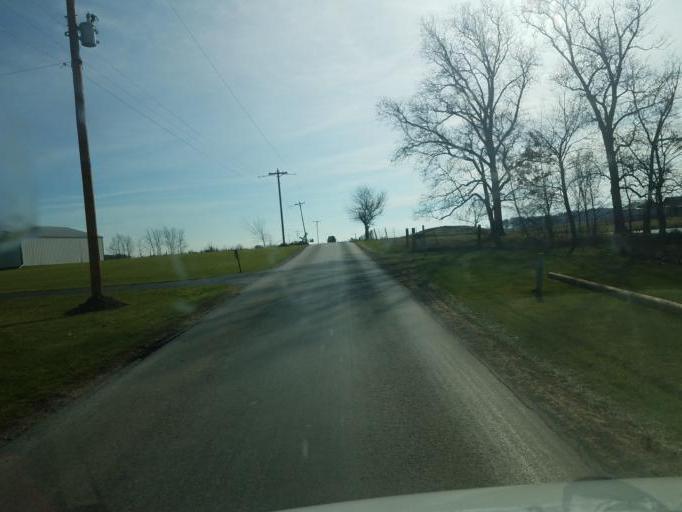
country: US
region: Ohio
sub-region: Hardin County
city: Kenton
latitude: 40.5772
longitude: -83.4538
